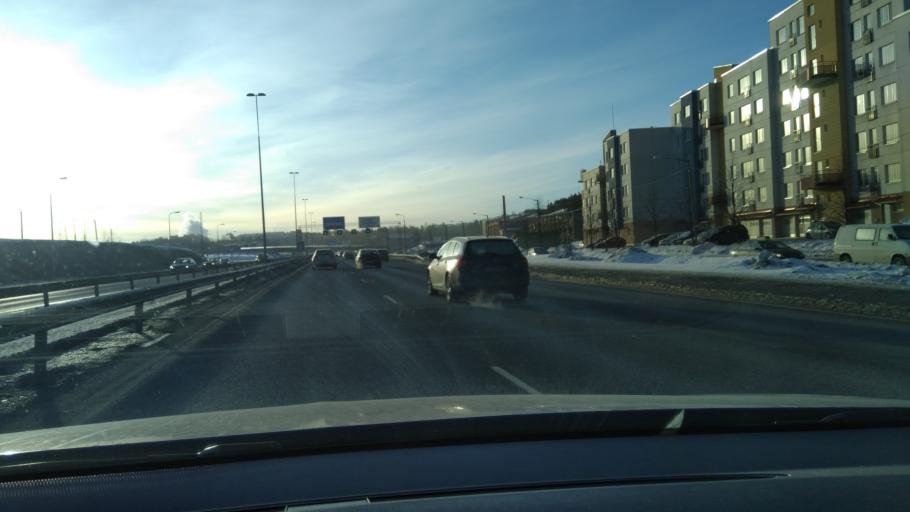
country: FI
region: Pirkanmaa
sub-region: Tampere
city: Tampere
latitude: 61.5052
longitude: 23.7179
